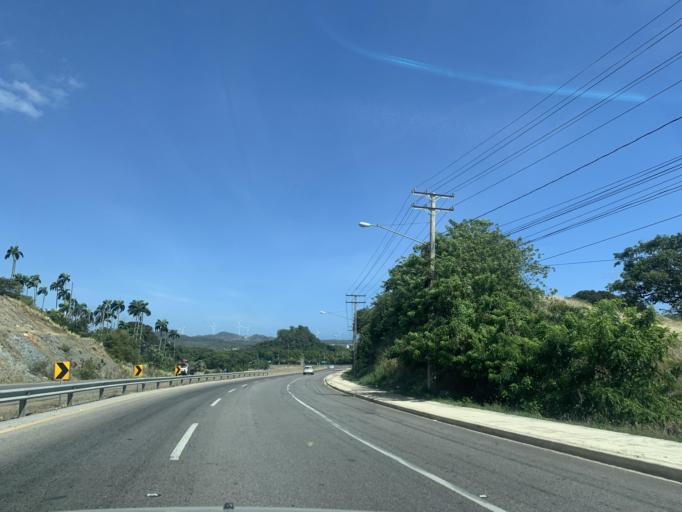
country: DO
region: Puerto Plata
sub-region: Puerto Plata
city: Puerto Plata
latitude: 19.8274
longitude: -70.7593
